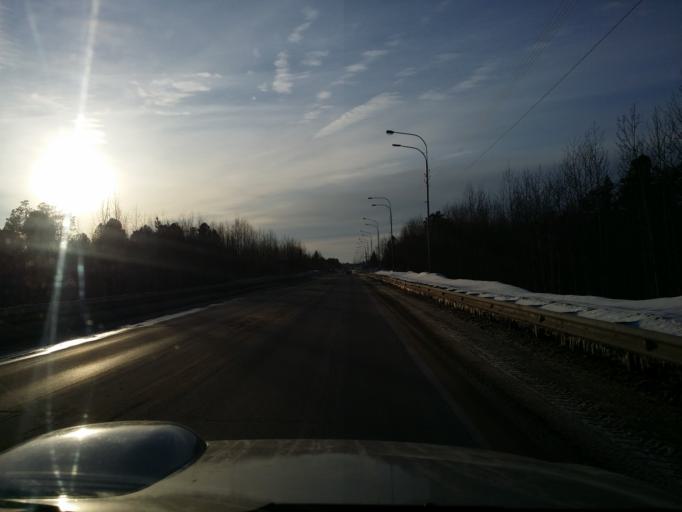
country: RU
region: Khanty-Mansiyskiy Avtonomnyy Okrug
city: Izluchinsk
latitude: 60.9645
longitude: 76.8645
